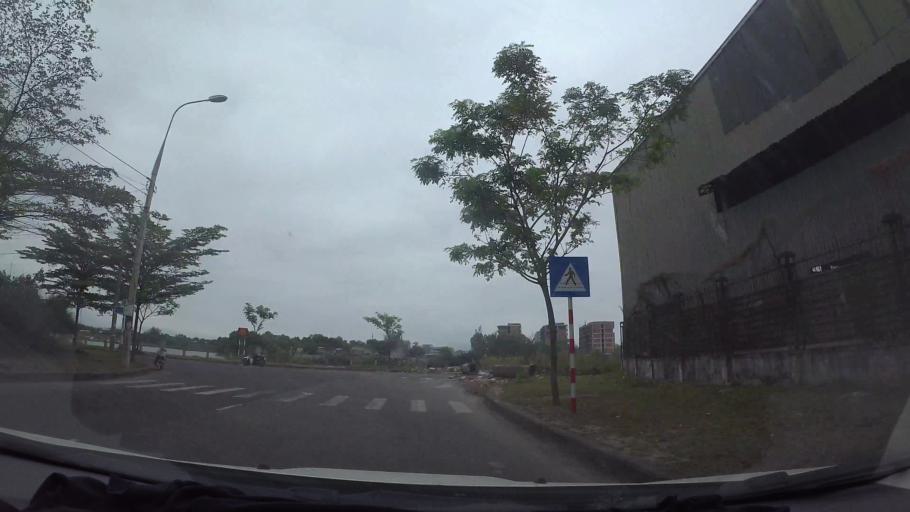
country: VN
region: Da Nang
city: Lien Chieu
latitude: 16.0880
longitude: 108.1377
